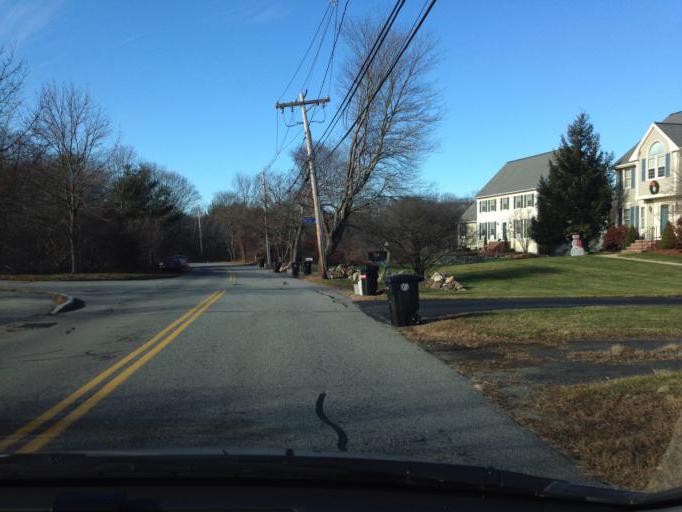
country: US
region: Massachusetts
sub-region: Middlesex County
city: Bedford
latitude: 42.4944
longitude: -71.3032
